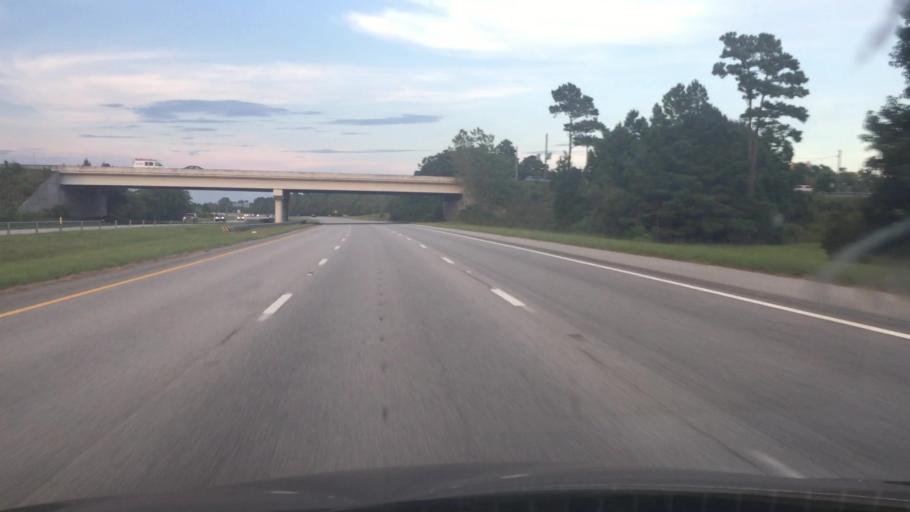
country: US
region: South Carolina
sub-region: Horry County
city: Myrtle Beach
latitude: 33.7535
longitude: -78.8541
